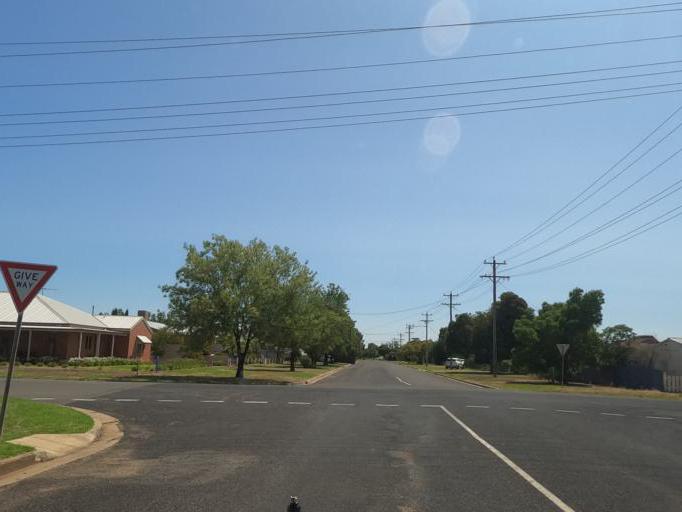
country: AU
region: New South Wales
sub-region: Corowa Shire
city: Mulwala
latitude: -35.9857
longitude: 146.0070
